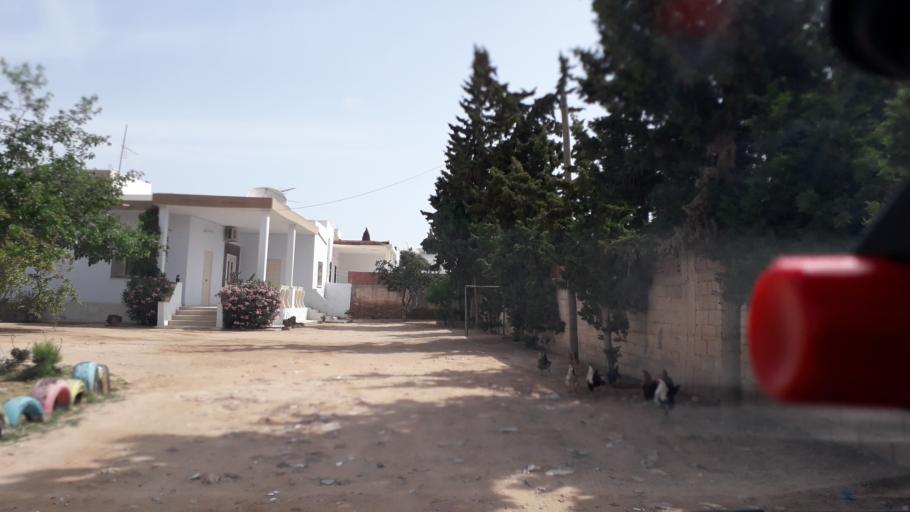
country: TN
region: Safaqis
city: Al Qarmadah
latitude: 34.7997
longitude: 10.7715
